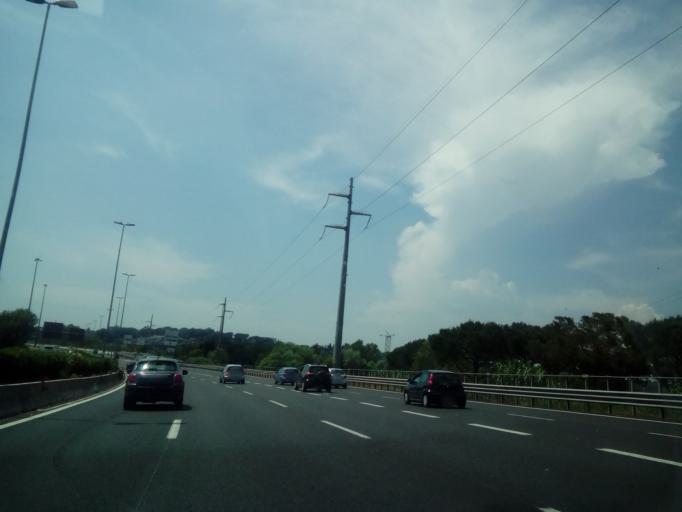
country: IT
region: Latium
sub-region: Citta metropolitana di Roma Capitale
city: Monte Caminetto
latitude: 41.9907
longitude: 12.5083
